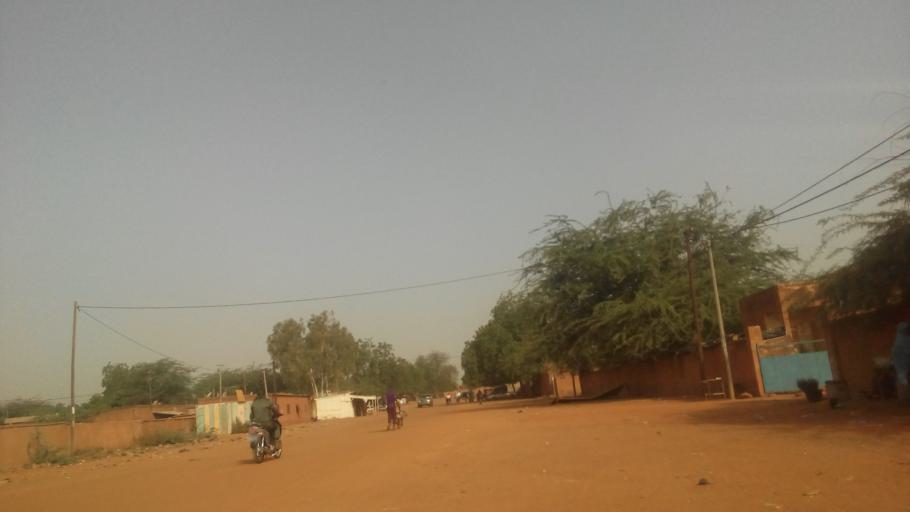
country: NE
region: Niamey
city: Niamey
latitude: 13.5285
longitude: 2.0880
